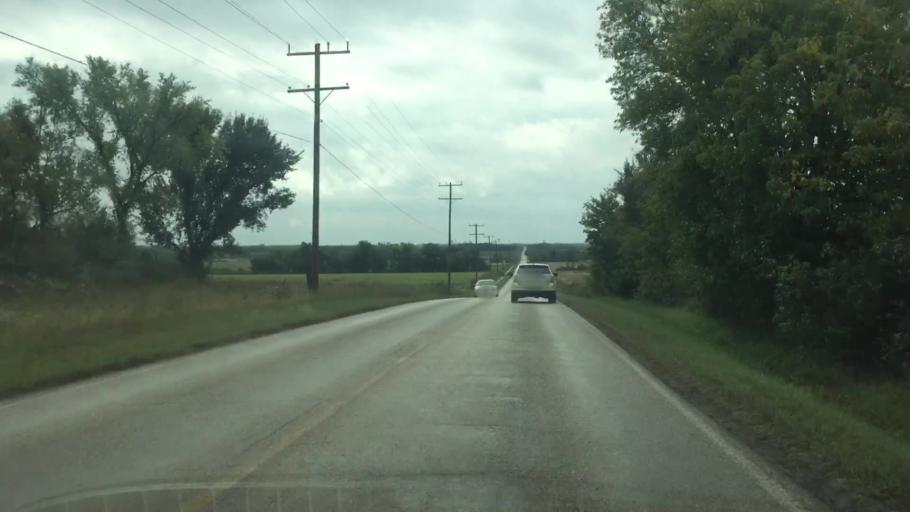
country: US
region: Kansas
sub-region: Allen County
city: Humboldt
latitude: 37.8602
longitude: -95.4369
